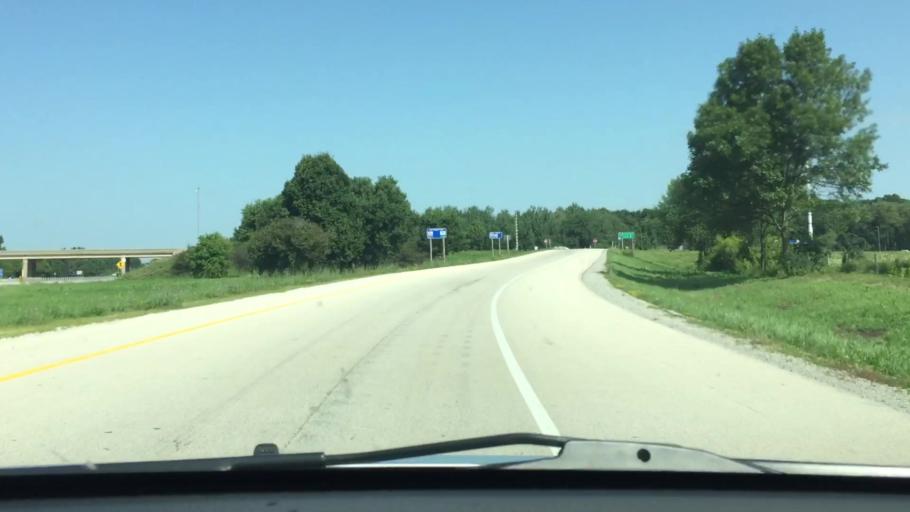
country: US
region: Wisconsin
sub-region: Jefferson County
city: Ixonia
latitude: 43.0740
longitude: -88.5895
